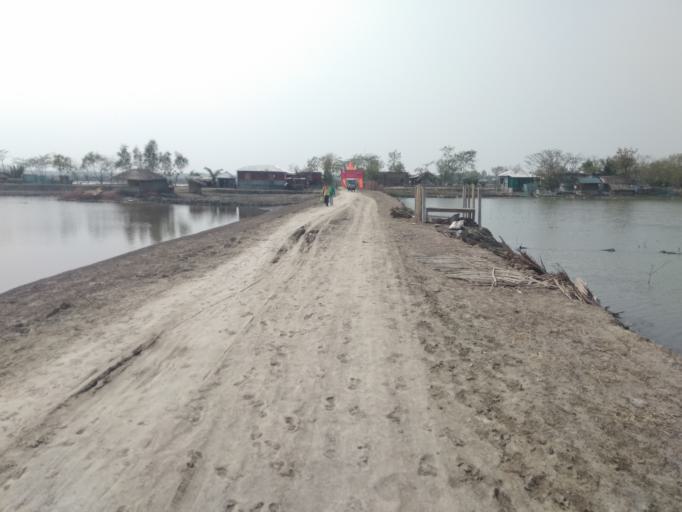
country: IN
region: West Bengal
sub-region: North 24 Parganas
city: Taki
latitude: 22.3475
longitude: 89.2236
